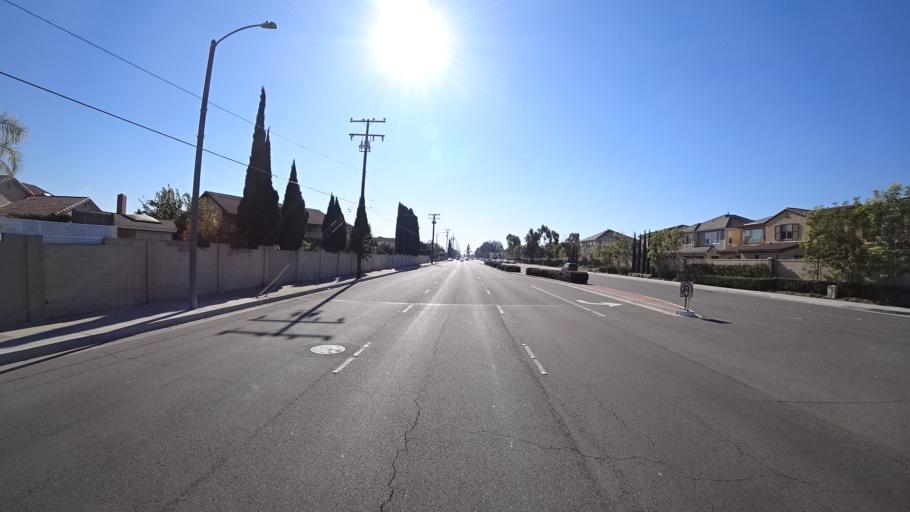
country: US
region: California
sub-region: Orange County
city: Garden Grove
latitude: 33.7477
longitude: -117.9548
